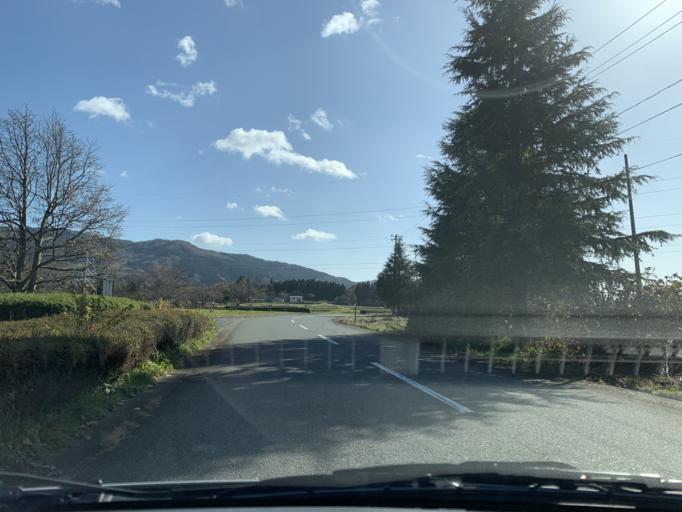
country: JP
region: Iwate
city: Mizusawa
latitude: 39.0258
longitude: 141.1235
